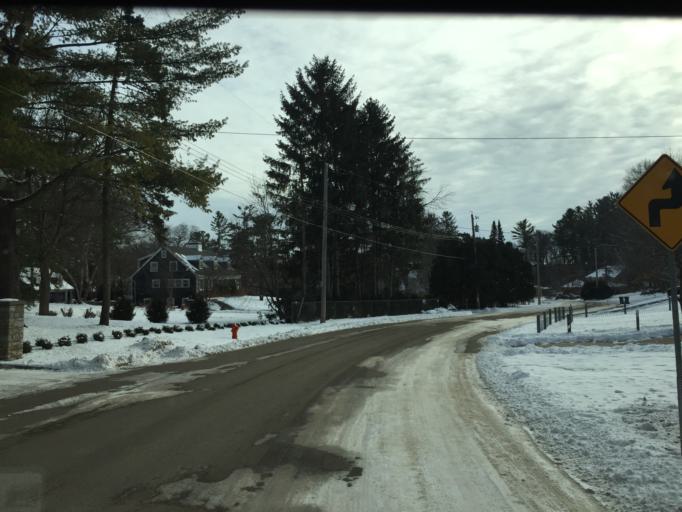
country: US
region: Minnesota
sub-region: Olmsted County
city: Rochester
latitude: 44.0134
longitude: -92.4784
